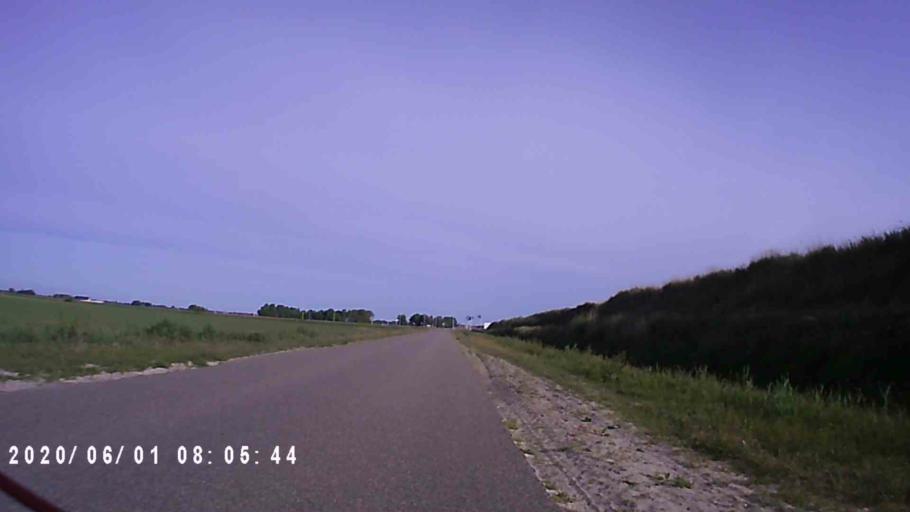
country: NL
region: Friesland
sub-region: Gemeente Tytsjerksteradiel
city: Oentsjerk
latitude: 53.2801
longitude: 5.9093
